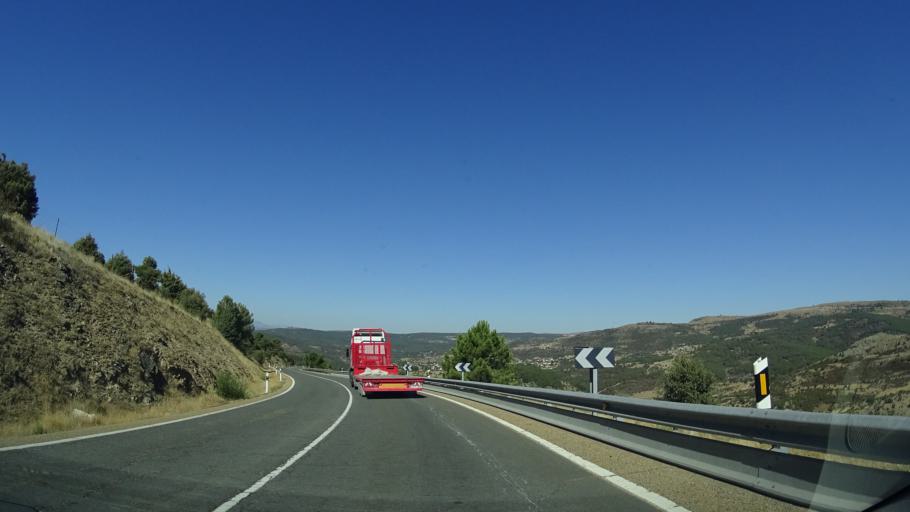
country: ES
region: Madrid
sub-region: Provincia de Madrid
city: Santa Maria de la Alameda
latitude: 40.5616
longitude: -4.2345
